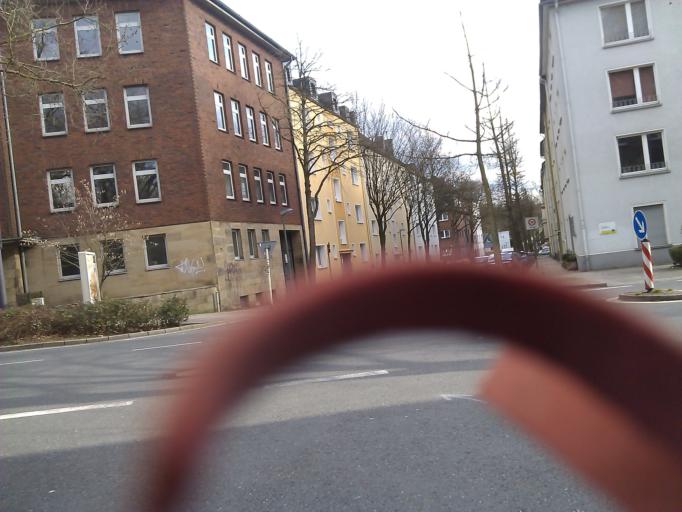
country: DE
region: North Rhine-Westphalia
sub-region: Regierungsbezirk Dusseldorf
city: Essen
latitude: 51.4494
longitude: 7.0258
